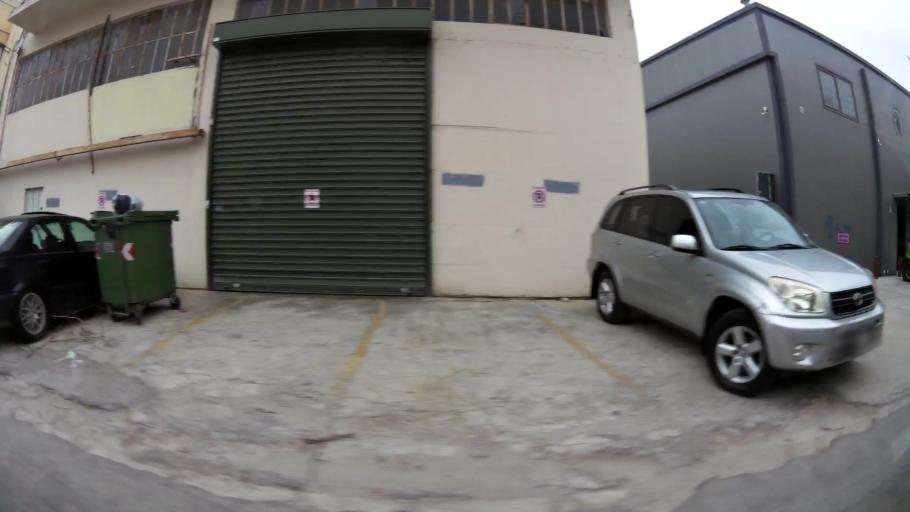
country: GR
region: Attica
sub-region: Nomarchia Athinas
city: Peristeri
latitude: 38.0144
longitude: 23.7112
